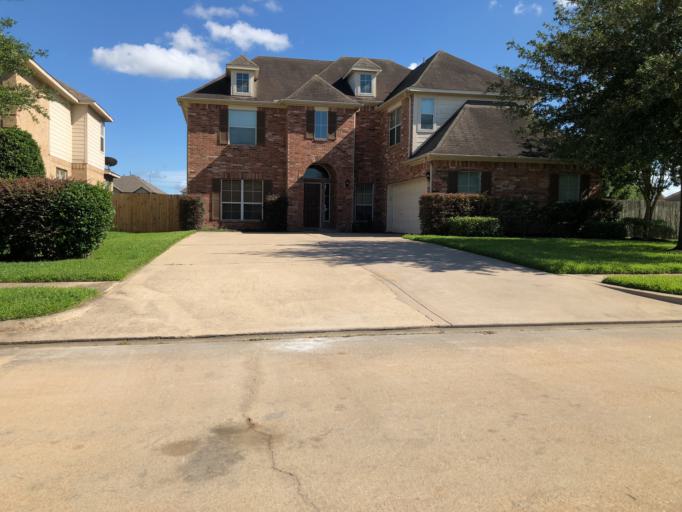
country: US
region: Texas
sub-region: Harris County
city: Katy
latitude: 29.8064
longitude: -95.8325
